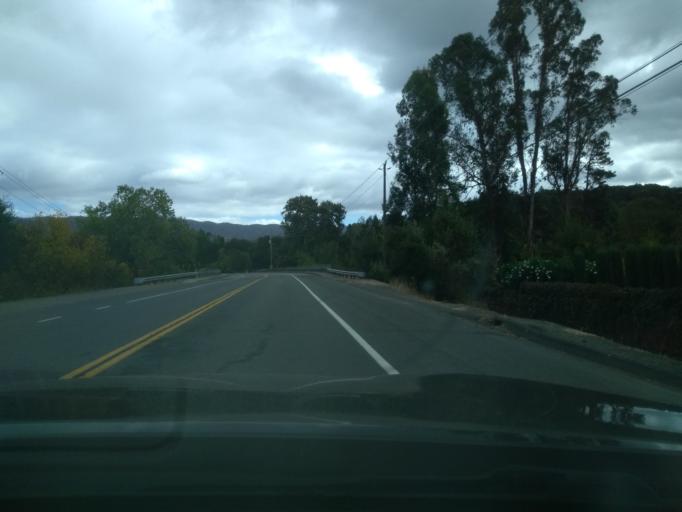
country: US
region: California
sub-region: Mendocino County
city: Ukiah
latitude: 39.1956
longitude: -123.1962
